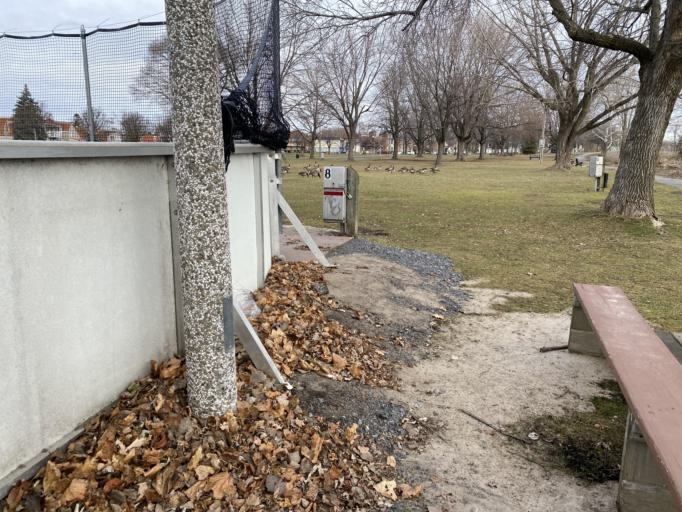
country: CA
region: Quebec
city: Saint-Raymond
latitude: 45.4268
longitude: -73.5951
